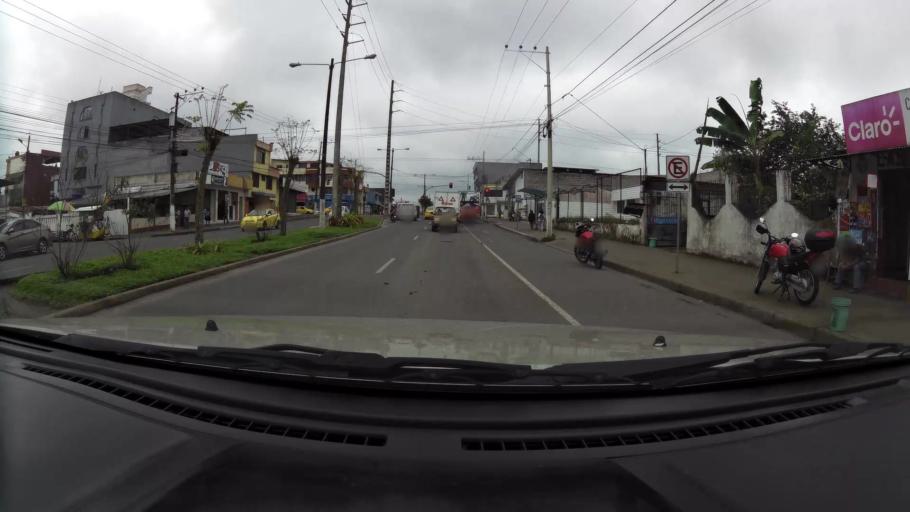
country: EC
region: Santo Domingo de los Tsachilas
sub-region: Canton Santo Domingo de los Colorados
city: Santo Domingo de los Colorados
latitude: -0.2632
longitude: -79.1660
